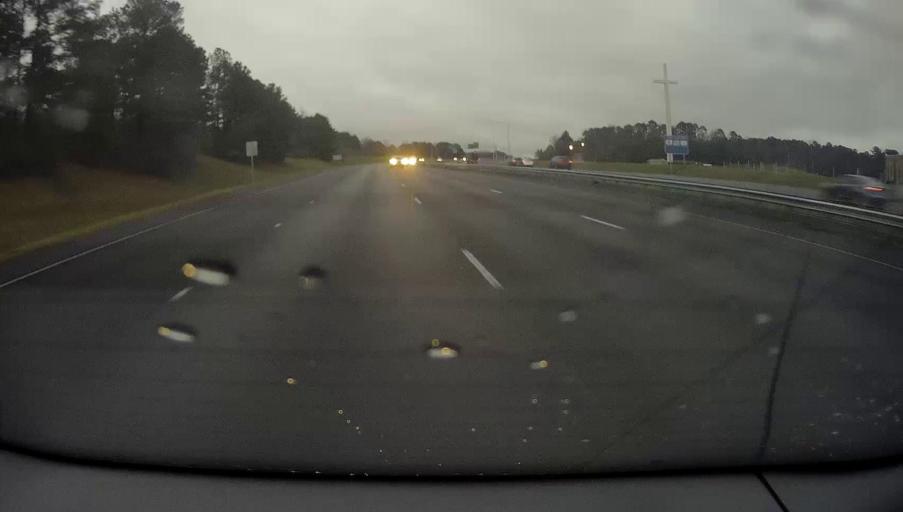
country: US
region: Alabama
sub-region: Jefferson County
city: Gardendale
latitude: 33.6627
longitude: -86.8312
